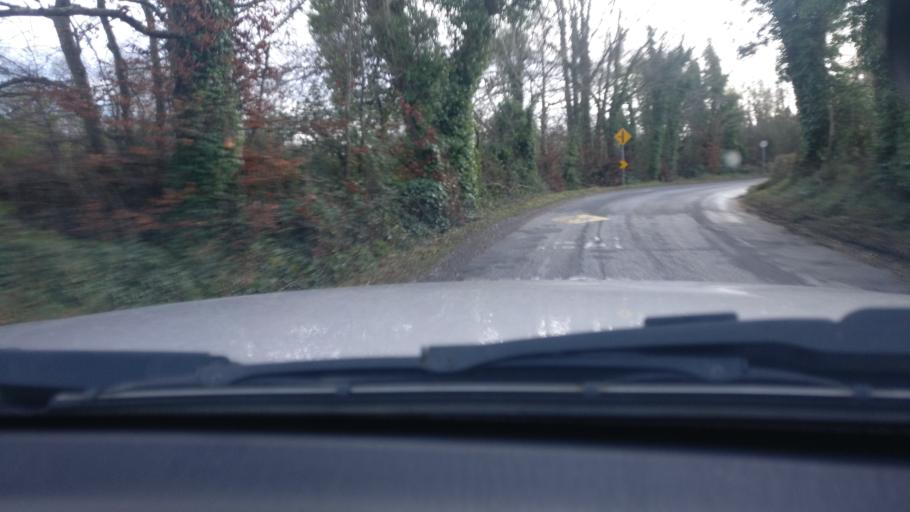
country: IE
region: Connaught
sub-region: County Galway
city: Ballinasloe
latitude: 53.2778
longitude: -8.2422
